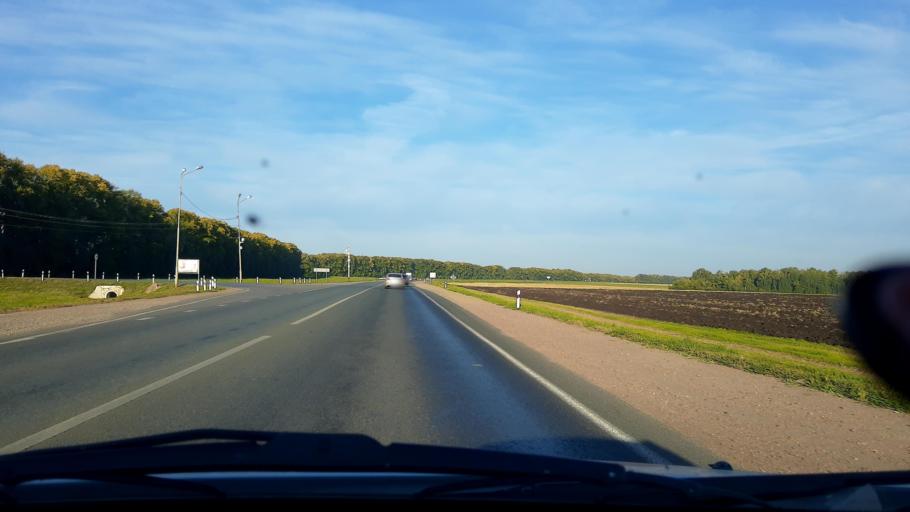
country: RU
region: Bashkortostan
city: Karmaskaly
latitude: 54.3853
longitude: 56.1535
